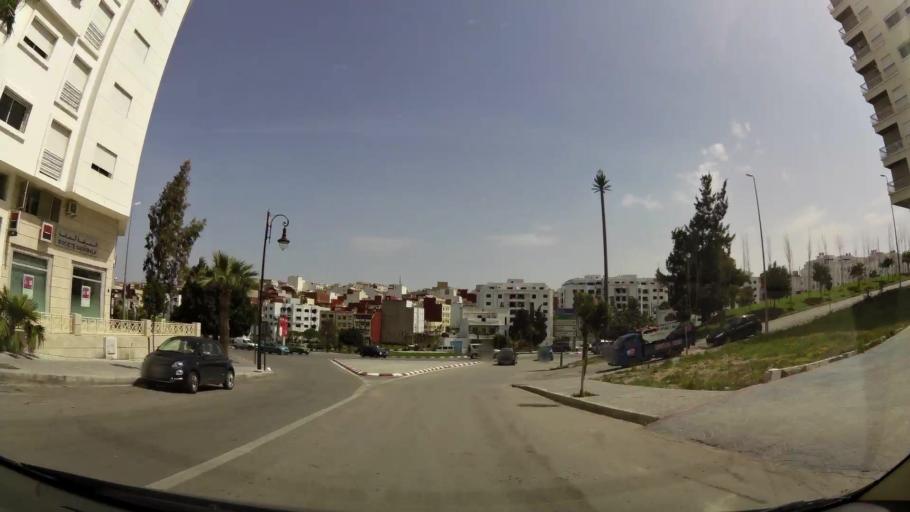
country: MA
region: Tanger-Tetouan
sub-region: Tanger-Assilah
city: Tangier
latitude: 35.7552
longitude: -5.8327
